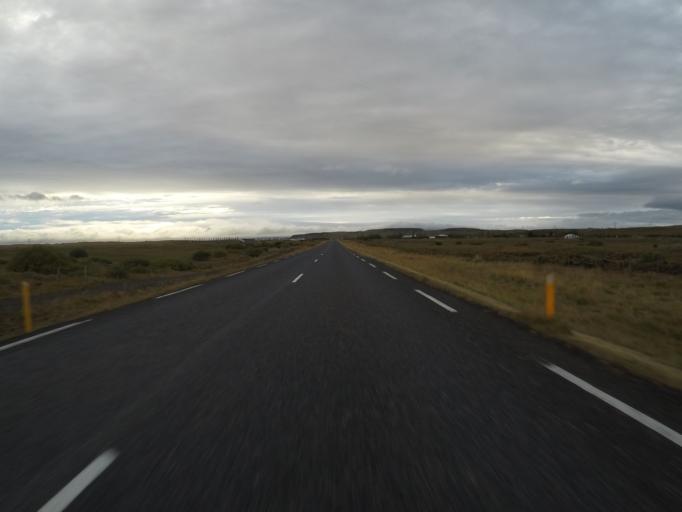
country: IS
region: South
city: Vestmannaeyjar
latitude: 64.0410
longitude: -20.2332
